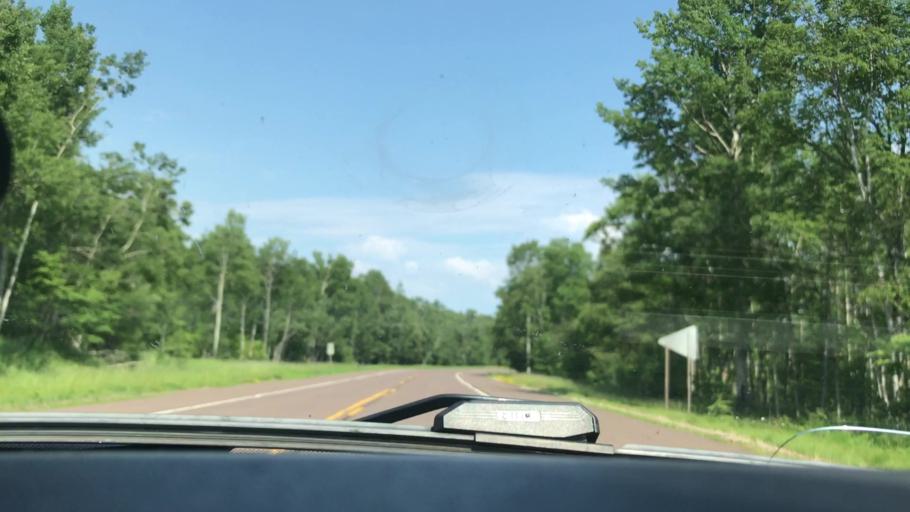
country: US
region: Minnesota
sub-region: Cook County
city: Grand Marais
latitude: 47.7775
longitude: -90.2193
